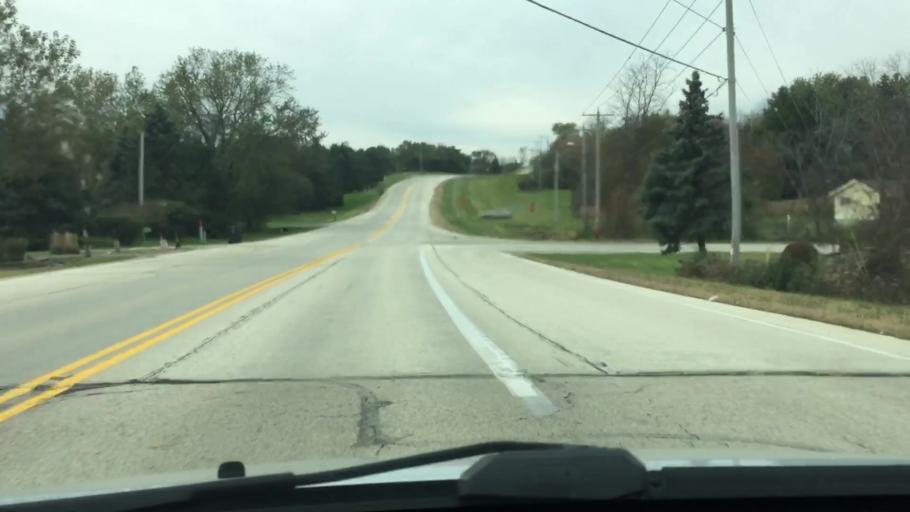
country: US
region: Wisconsin
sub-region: Waukesha County
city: Big Bend
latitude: 42.9056
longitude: -88.2444
